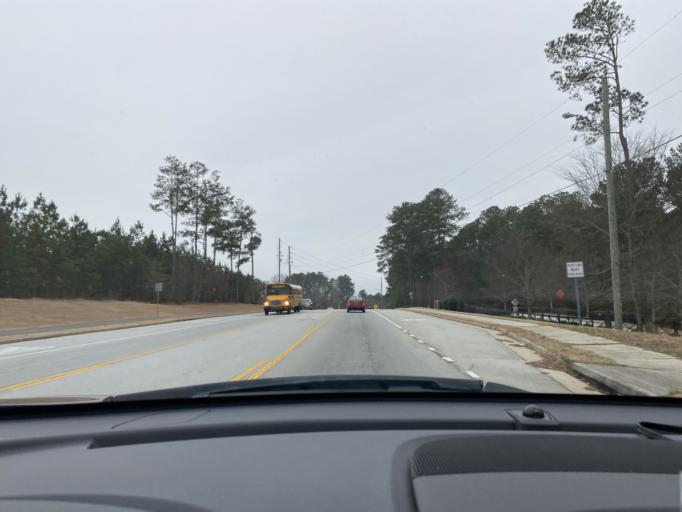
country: US
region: Georgia
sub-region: Gwinnett County
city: Grayson
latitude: 33.9176
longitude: -83.8948
